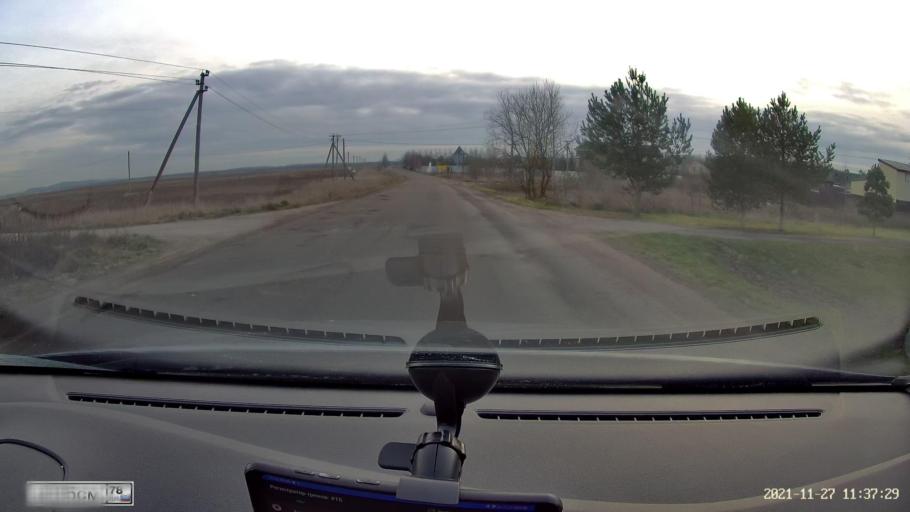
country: RU
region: Leningrad
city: Russko-Vysotskoye
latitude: 59.6938
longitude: 29.9878
